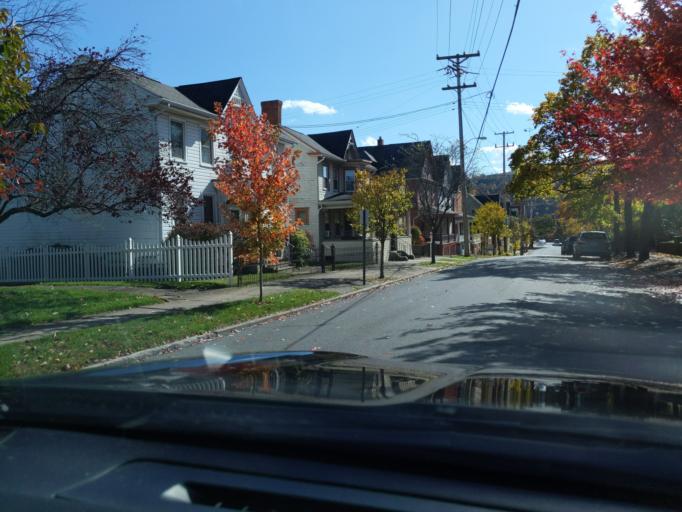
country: US
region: Pennsylvania
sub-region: Blair County
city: Hollidaysburg
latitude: 40.4309
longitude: -78.3959
